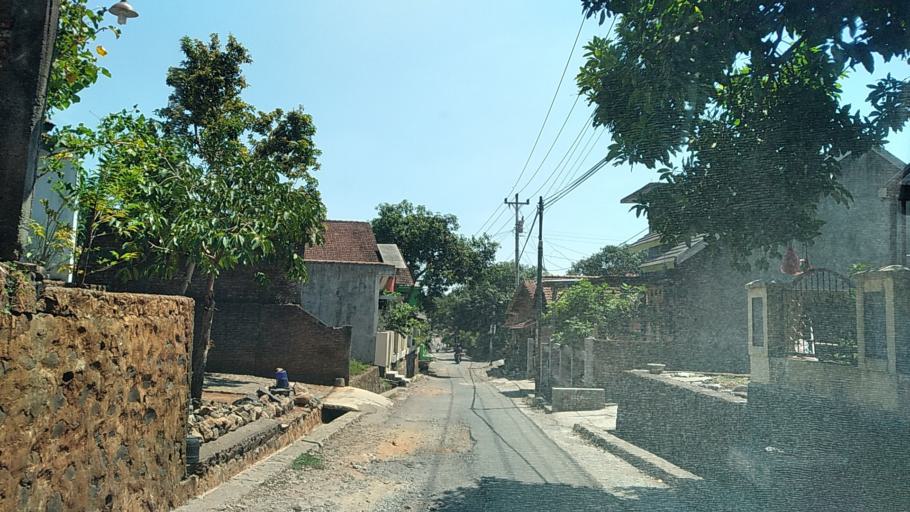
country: ID
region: Central Java
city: Ungaran
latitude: -7.1018
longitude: 110.4116
